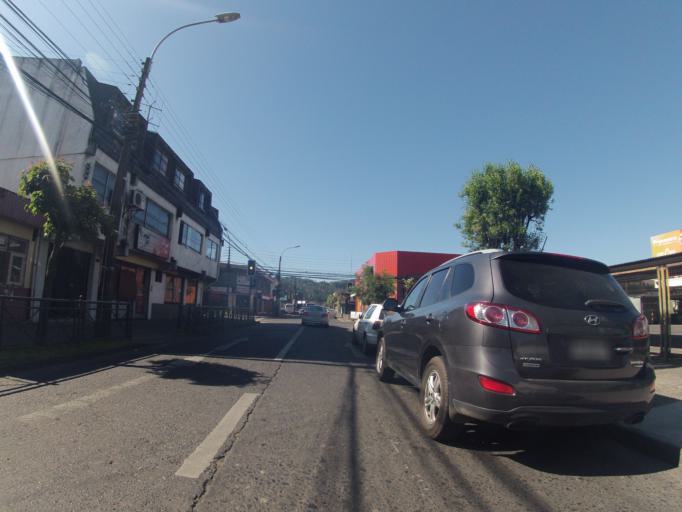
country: CL
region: Araucania
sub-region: Provincia de Cautin
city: Temuco
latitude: -38.7394
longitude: -72.5934
